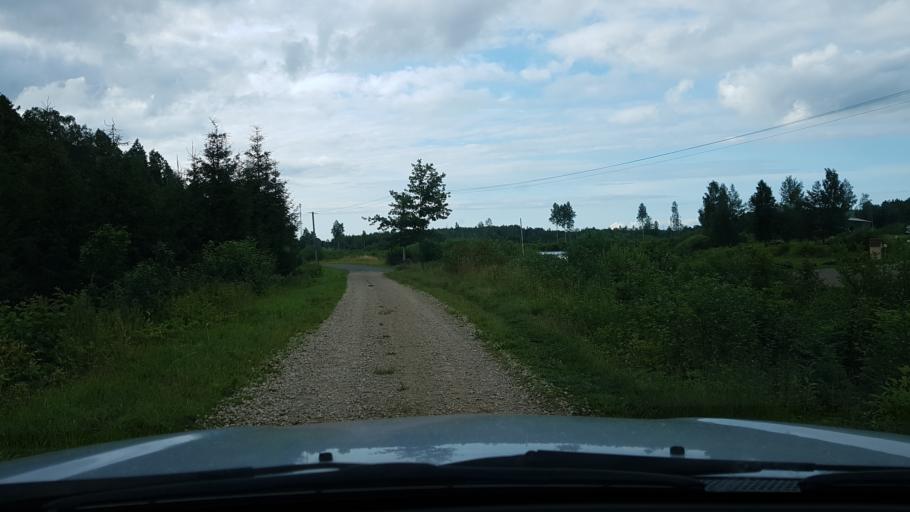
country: EE
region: Ida-Virumaa
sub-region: Narva-Joesuu linn
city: Narva-Joesuu
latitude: 59.3969
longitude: 27.9700
